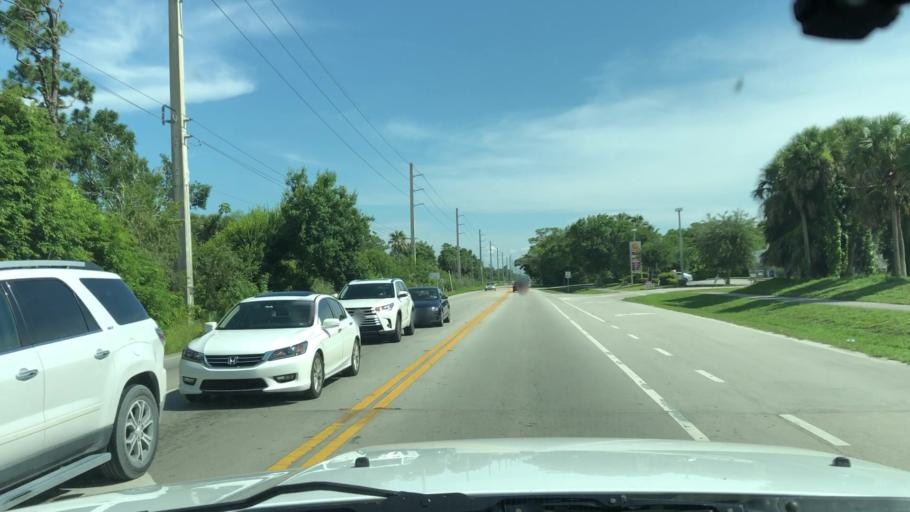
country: US
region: Florida
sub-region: Indian River County
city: Florida Ridge
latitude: 27.5867
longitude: -80.4143
